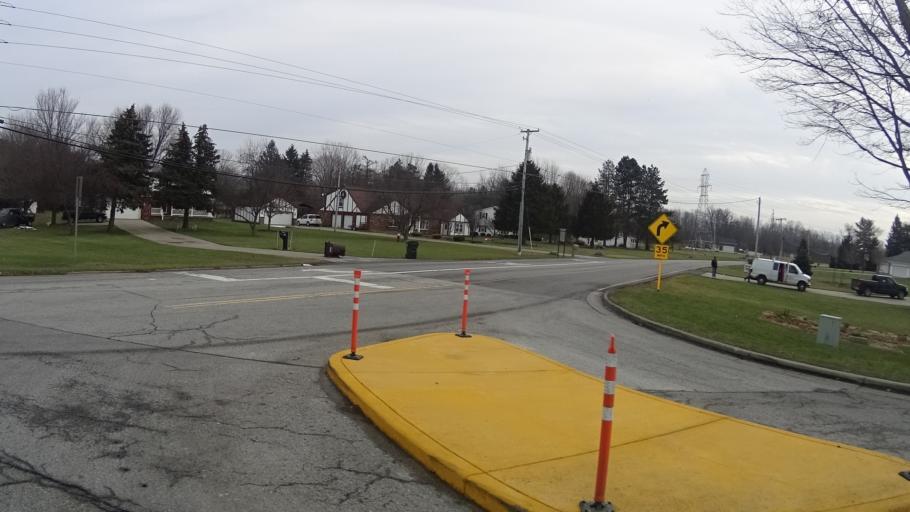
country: US
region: Ohio
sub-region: Lorain County
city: Amherst
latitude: 41.3960
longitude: -82.1899
